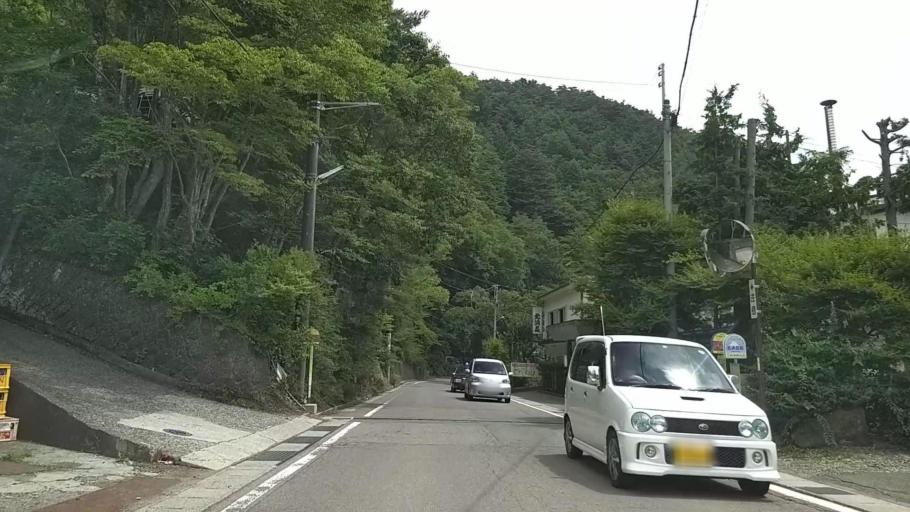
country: JP
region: Yamanashi
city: Fujikawaguchiko
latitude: 35.5238
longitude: 138.7494
